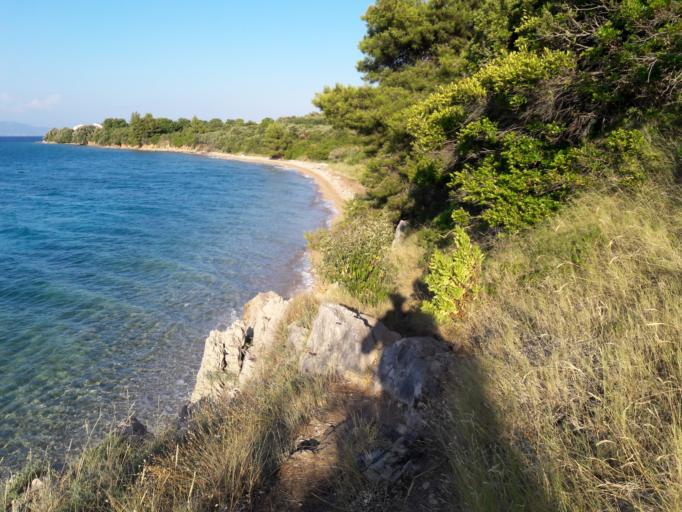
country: HR
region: Dubrovacko-Neretvanska
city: Orebic
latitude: 43.0231
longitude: 17.1606
